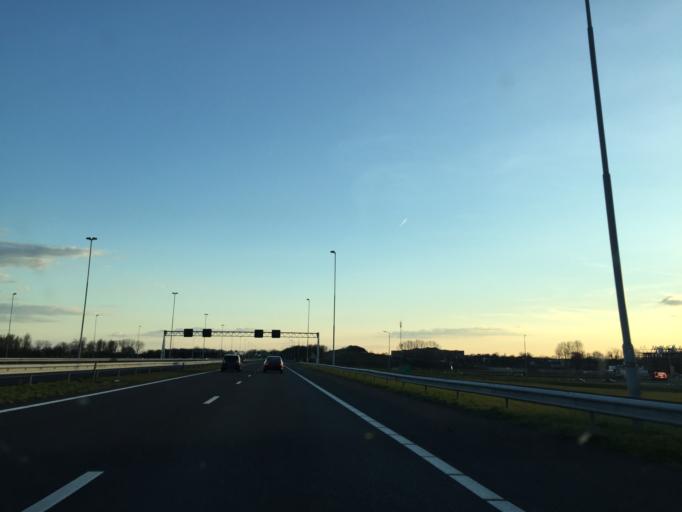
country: NL
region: North Brabant
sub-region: Gemeente Tilburg
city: Tilburg
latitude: 51.5455
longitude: 5.1161
